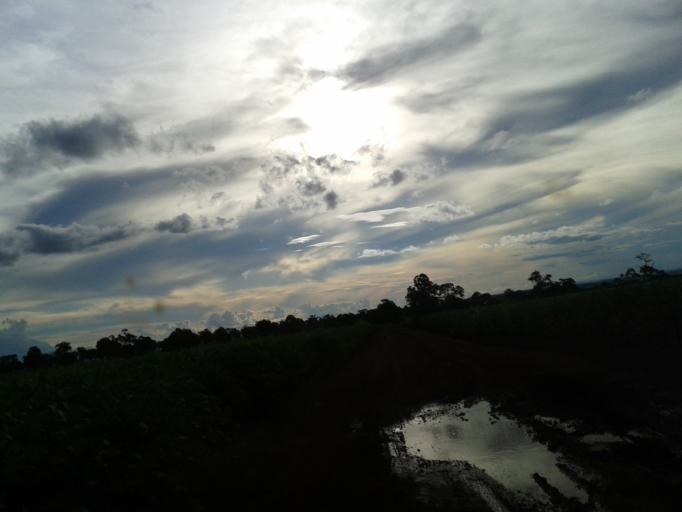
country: BR
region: Minas Gerais
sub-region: Capinopolis
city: Capinopolis
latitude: -18.7453
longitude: -49.8093
